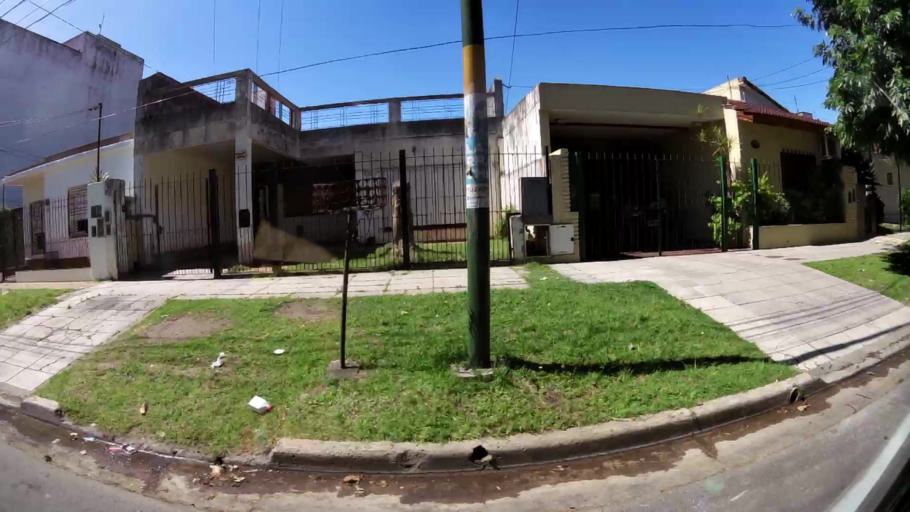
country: AR
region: Buenos Aires
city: Ituzaingo
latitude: -34.6653
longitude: -58.6675
